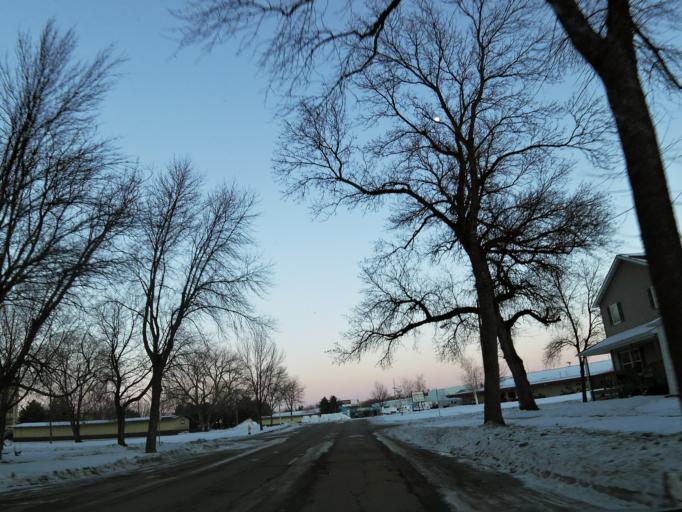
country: US
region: North Dakota
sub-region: Grand Forks County
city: Grand Forks
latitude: 47.9211
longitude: -97.0412
